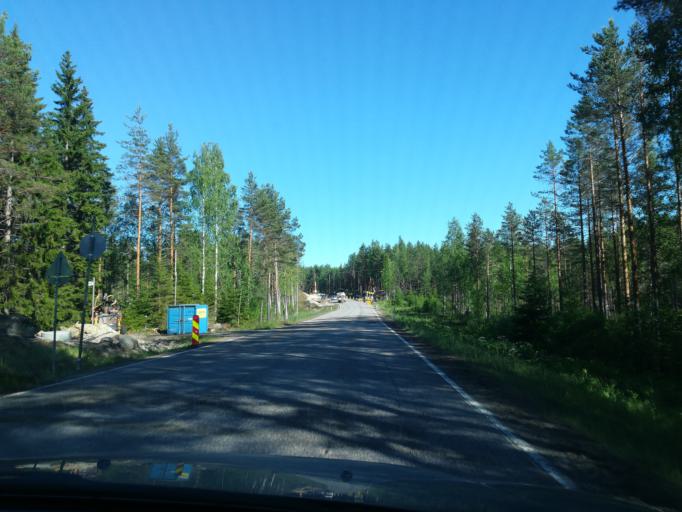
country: FI
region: Southern Savonia
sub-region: Mikkeli
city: Puumala
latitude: 61.4689
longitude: 28.3159
